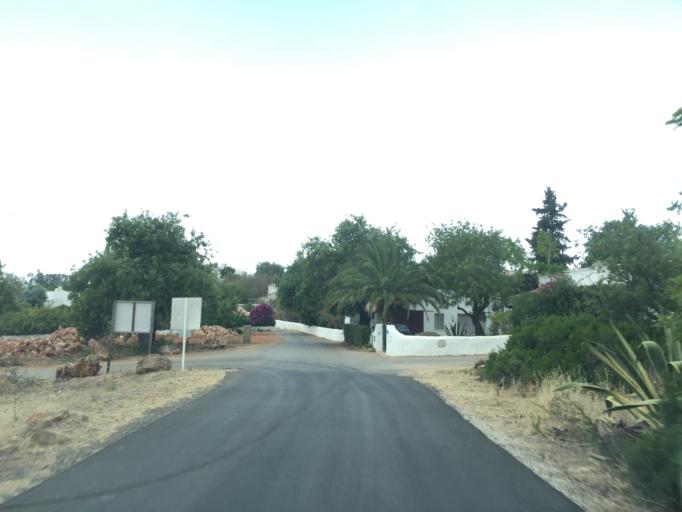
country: PT
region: Faro
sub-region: Loule
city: Almancil
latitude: 37.0996
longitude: -8.0375
